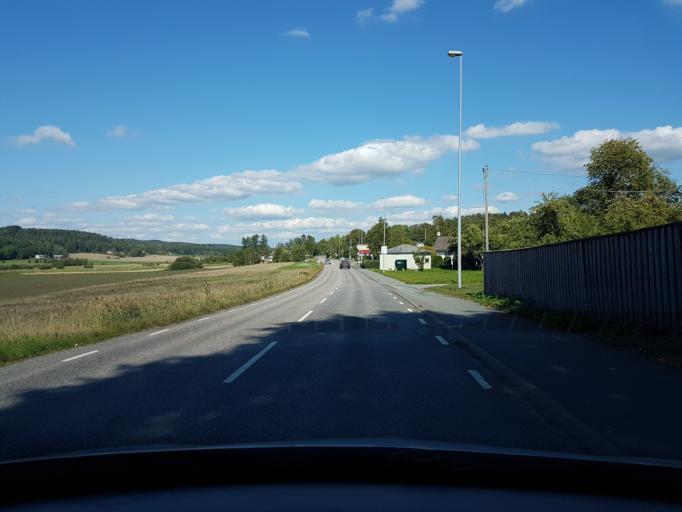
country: SE
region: Vaestra Goetaland
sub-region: Ale Kommun
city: Skepplanda
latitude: 57.9816
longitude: 12.2025
